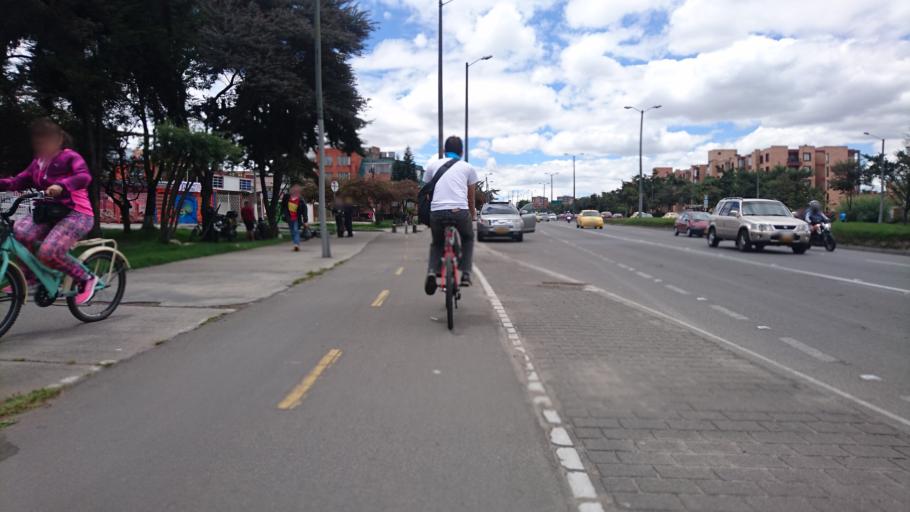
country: CO
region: Bogota D.C.
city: Bogota
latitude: 4.6688
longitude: -74.1279
